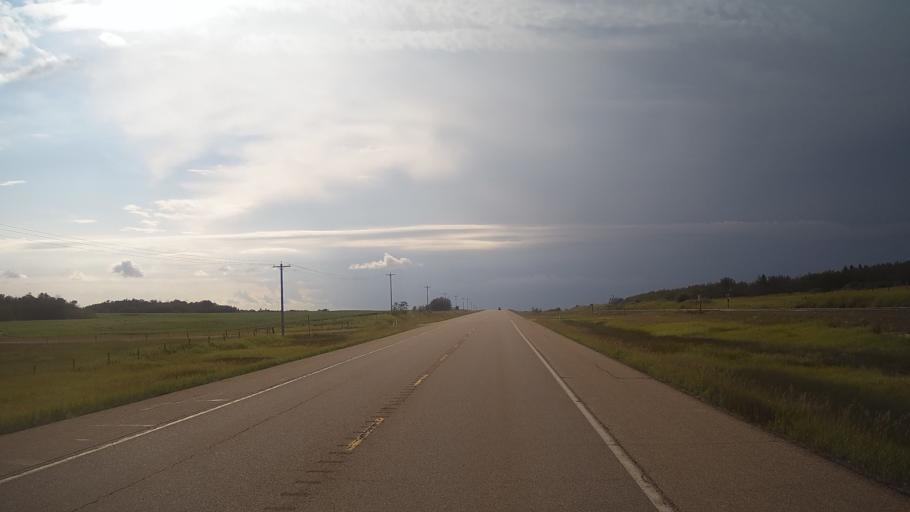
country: CA
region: Alberta
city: Viking
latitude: 53.1598
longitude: -112.0013
